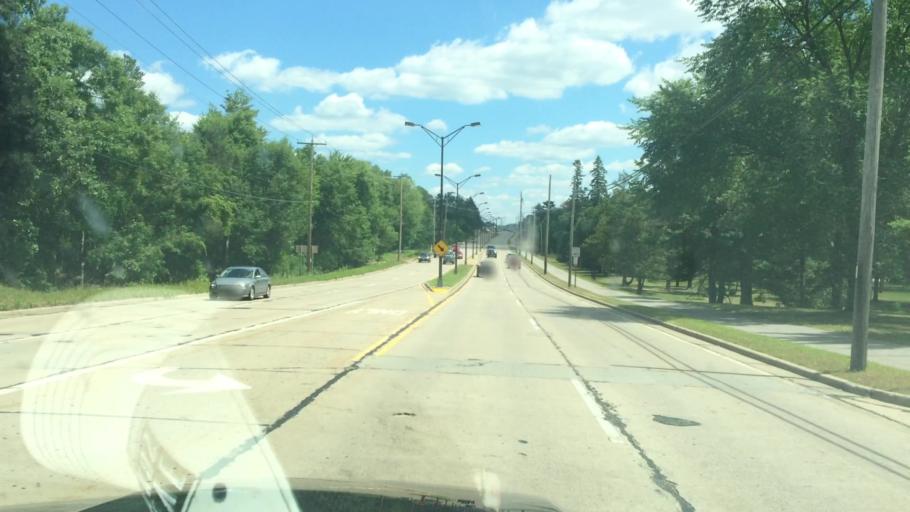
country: US
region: Wisconsin
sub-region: Portage County
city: Stevens Point
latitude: 44.5233
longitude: -89.5410
